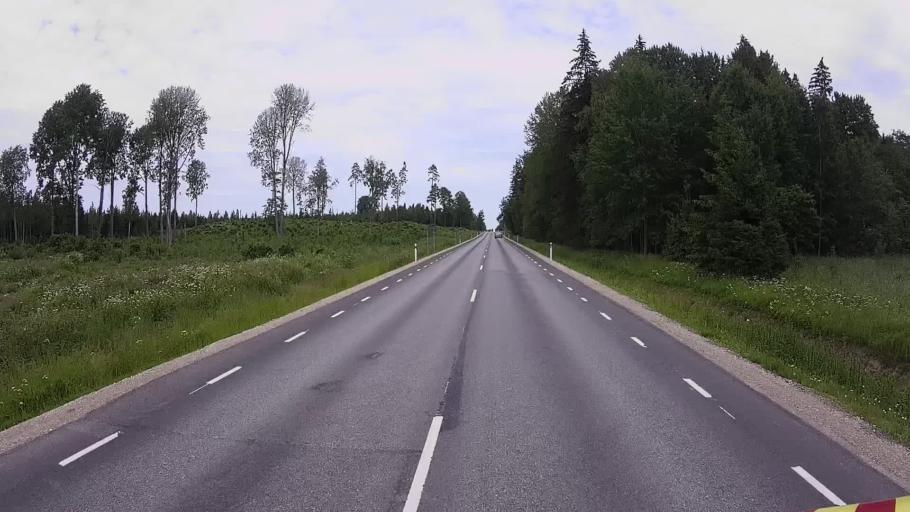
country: EE
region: Viljandimaa
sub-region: Viljandi linn
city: Viljandi
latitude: 58.2549
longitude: 25.5896
